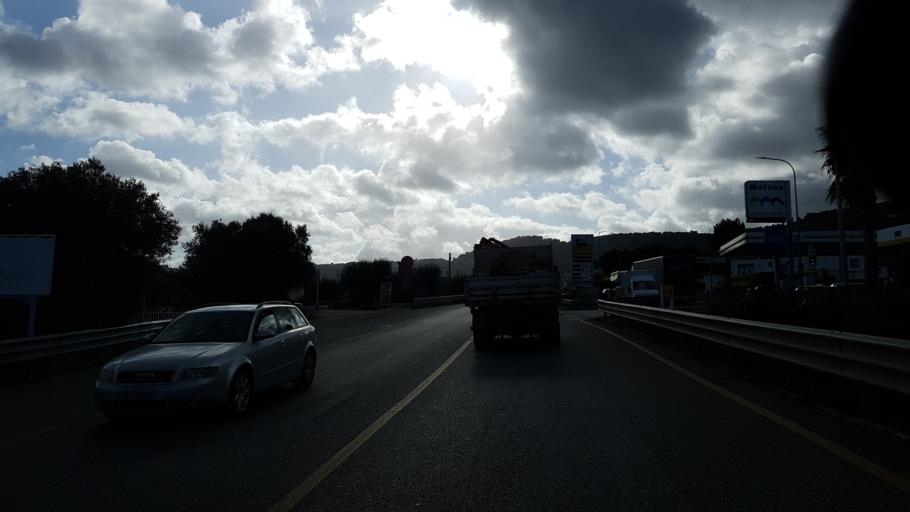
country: IT
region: Apulia
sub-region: Provincia di Brindisi
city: Fasano
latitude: 40.8255
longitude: 17.3494
